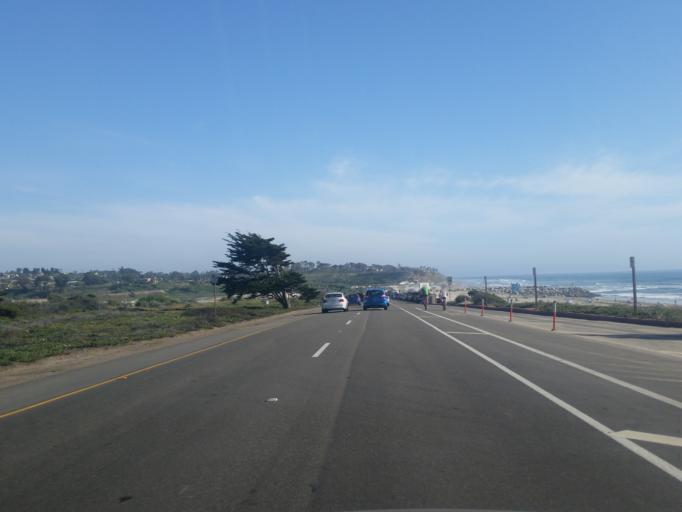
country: US
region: California
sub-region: San Diego County
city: Encinitas
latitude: 33.0908
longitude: -117.3140
